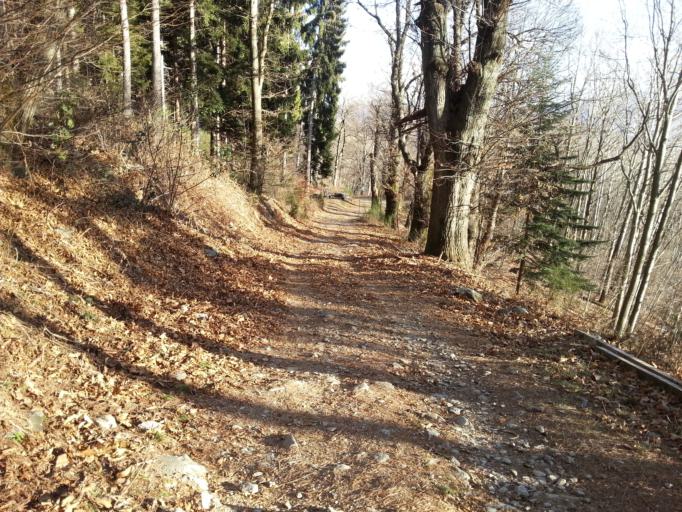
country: CH
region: Ticino
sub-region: Lugano District
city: Gravesano
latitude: 46.0417
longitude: 8.8646
